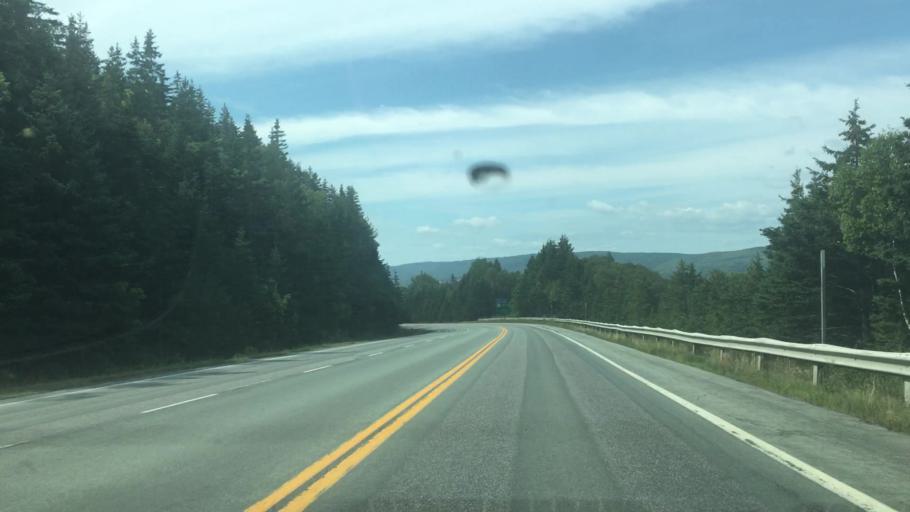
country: CA
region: Nova Scotia
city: Sydney Mines
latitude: 46.2456
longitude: -60.5559
